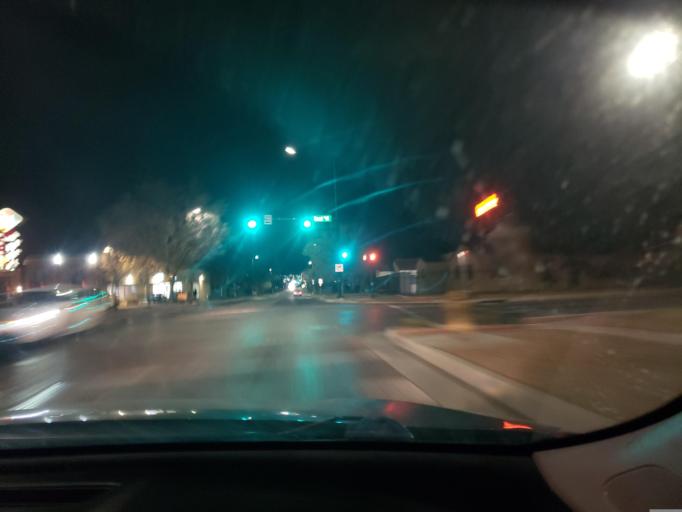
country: US
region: New Mexico
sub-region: Bernalillo County
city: Albuquerque
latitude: 35.0753
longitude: -106.6222
